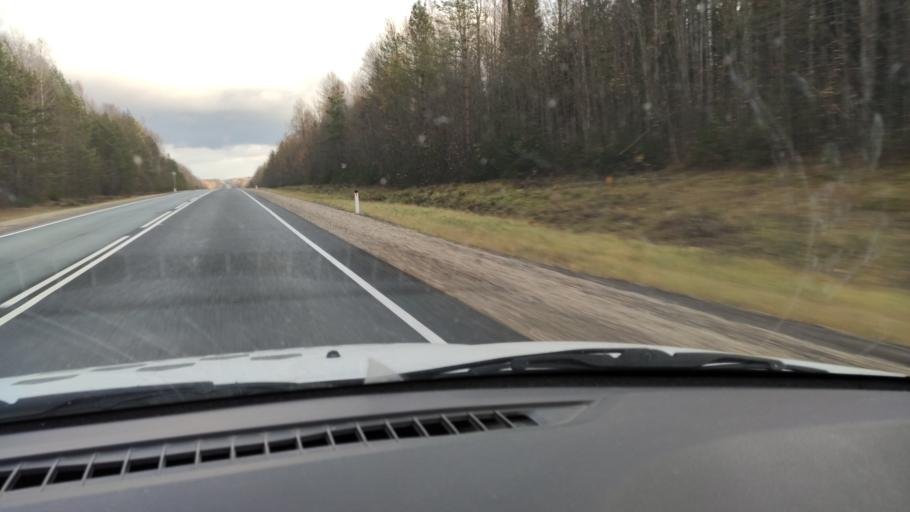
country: RU
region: Kirov
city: Chernaya Kholunitsa
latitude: 58.7979
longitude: 51.8688
